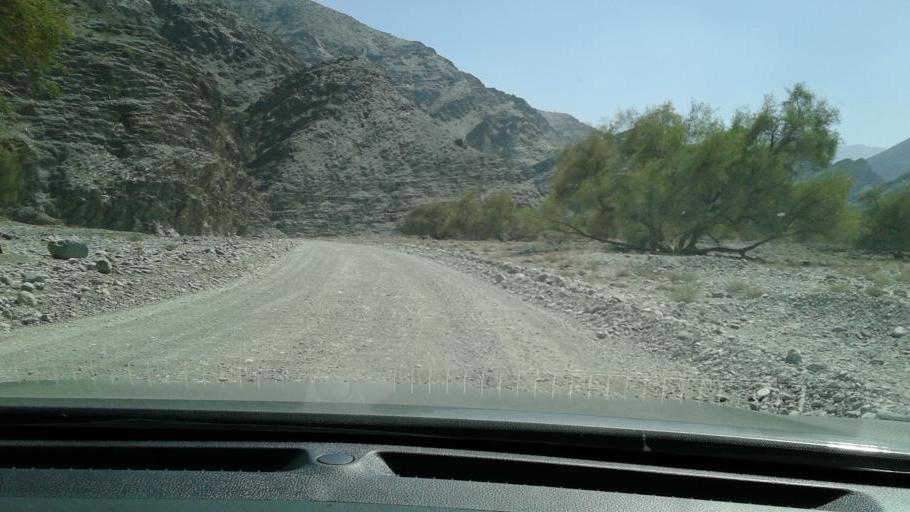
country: OM
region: Al Batinah
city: Bayt al `Awabi
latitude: 23.2658
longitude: 57.4465
